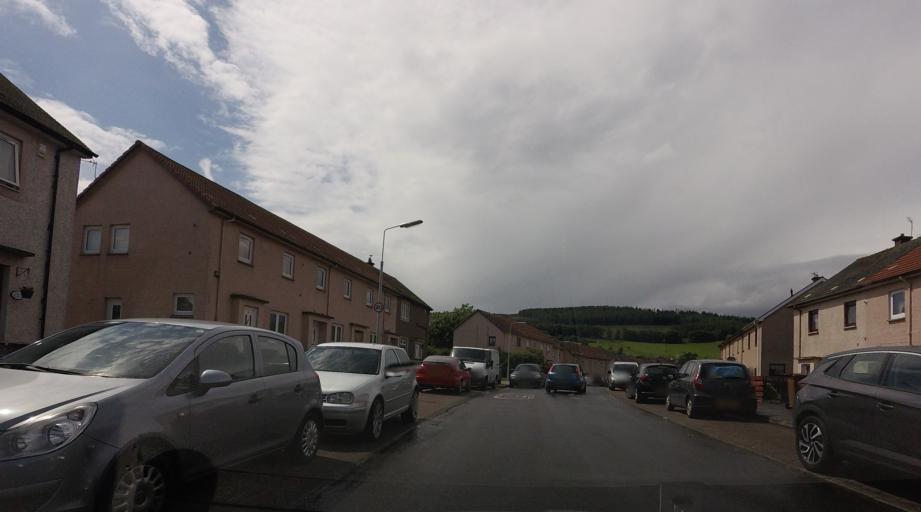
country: GB
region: Scotland
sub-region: Fife
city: Ballingry
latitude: 56.1617
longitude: -3.3276
